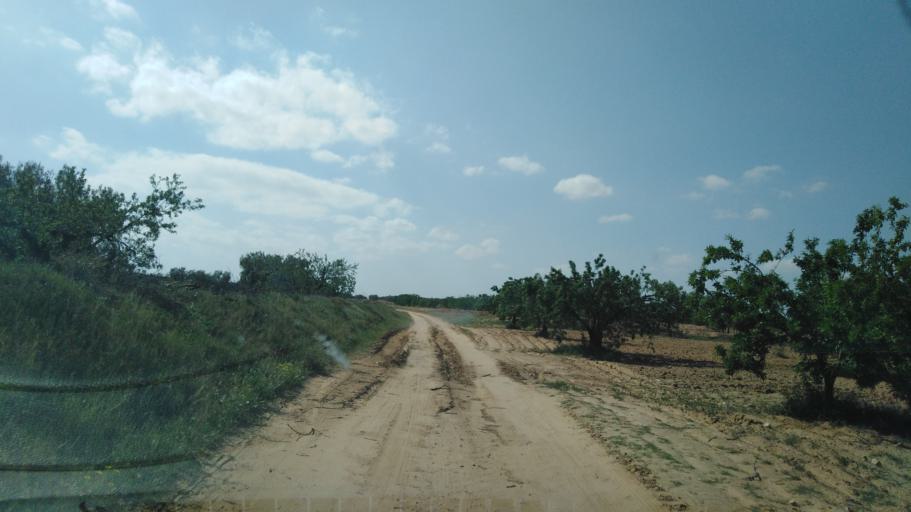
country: TN
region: Safaqis
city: Bi'r `Ali Bin Khalifah
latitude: 34.7906
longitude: 10.4041
